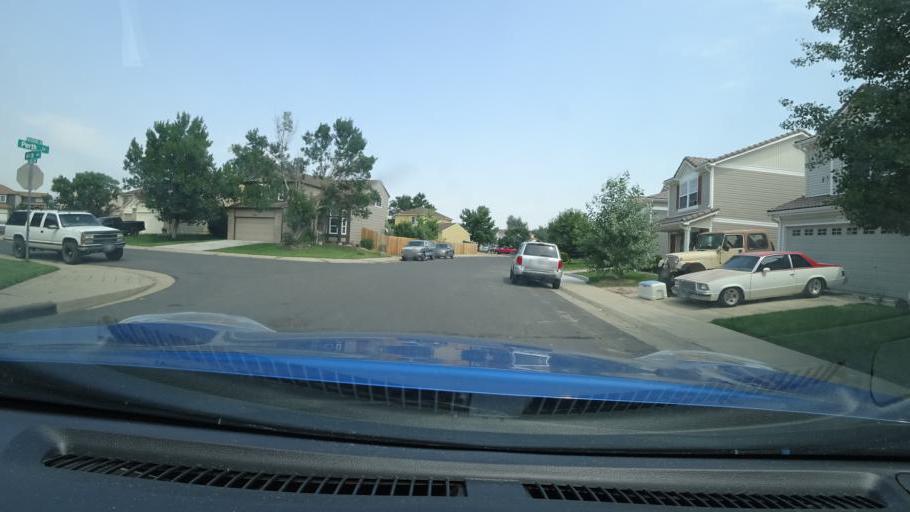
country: US
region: Colorado
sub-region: Adams County
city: Aurora
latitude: 39.7768
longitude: -104.7386
